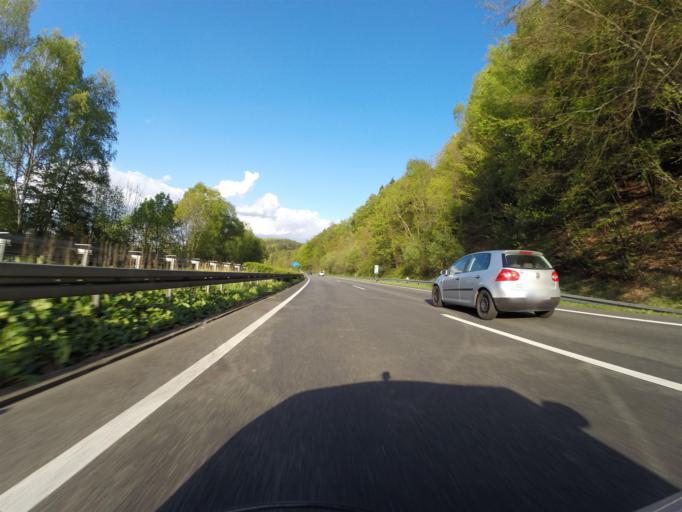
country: DE
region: Saarland
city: Sankt Ingbert
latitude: 49.2660
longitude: 7.1301
